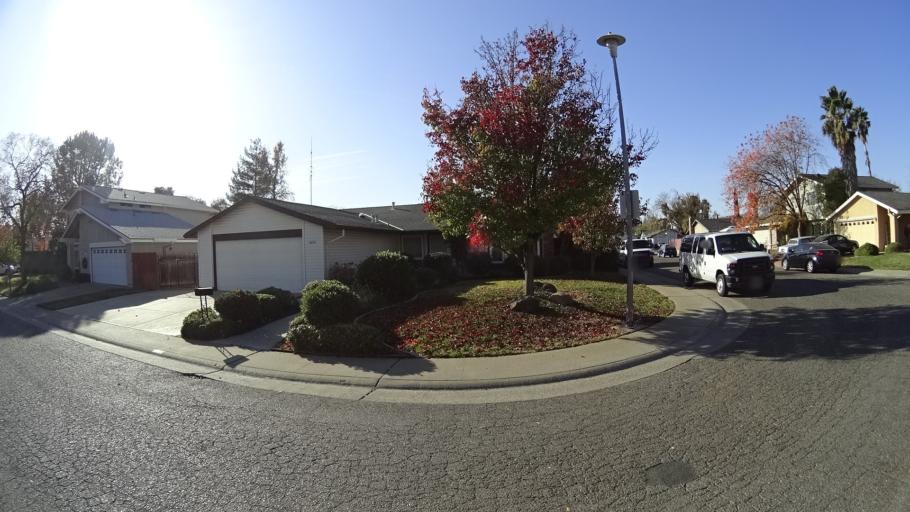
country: US
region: California
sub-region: Sacramento County
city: Antelope
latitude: 38.6982
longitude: -121.3096
